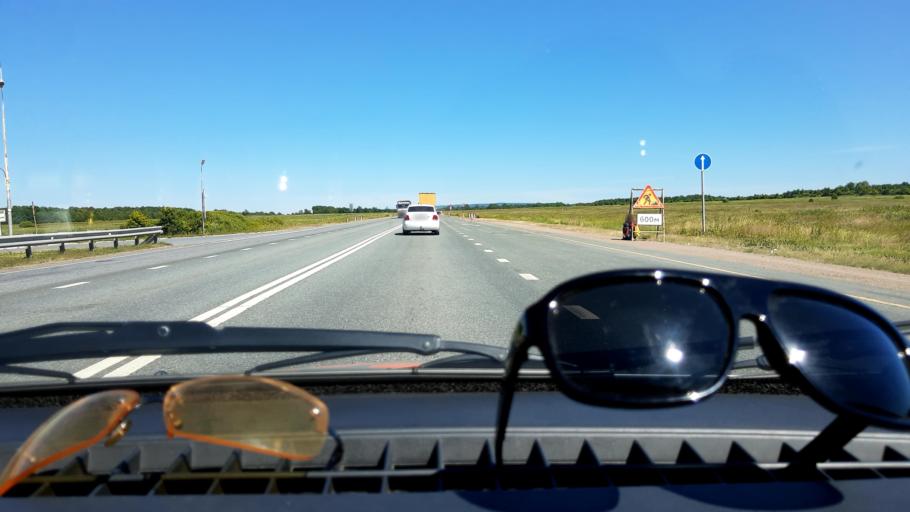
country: RU
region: Bashkortostan
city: Kudeyevskiy
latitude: 54.8171
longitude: 56.8045
